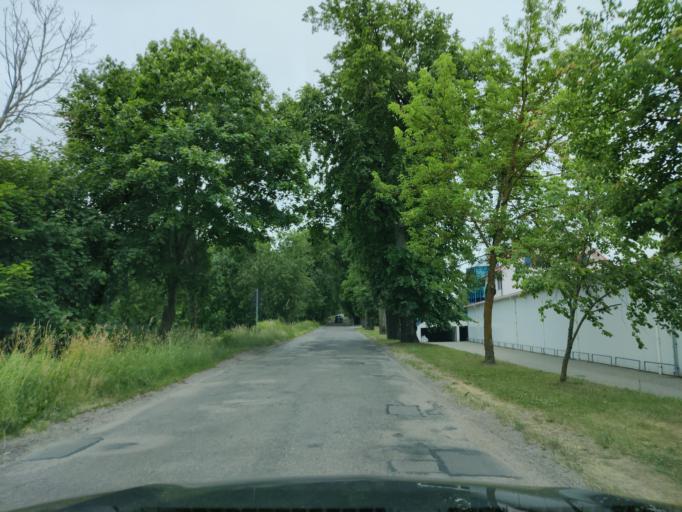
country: PL
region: Warmian-Masurian Voivodeship
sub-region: Powiat gizycki
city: Ryn
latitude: 53.9325
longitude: 21.5498
